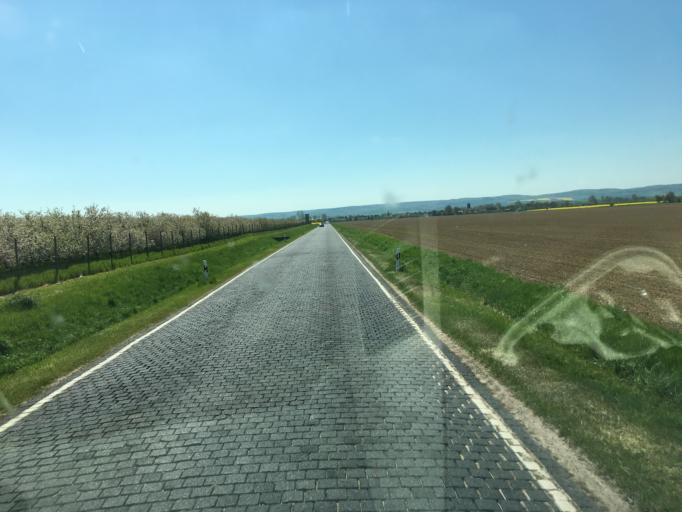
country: DE
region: Thuringia
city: Monchpfiffel-Nikolausrieth
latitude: 51.3719
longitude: 11.3712
